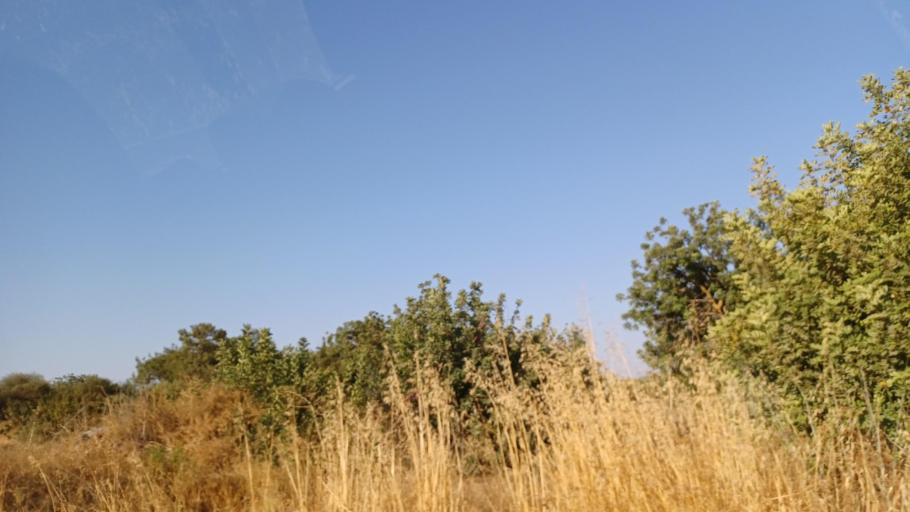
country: CY
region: Limassol
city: Pissouri
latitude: 34.7140
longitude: 32.6742
